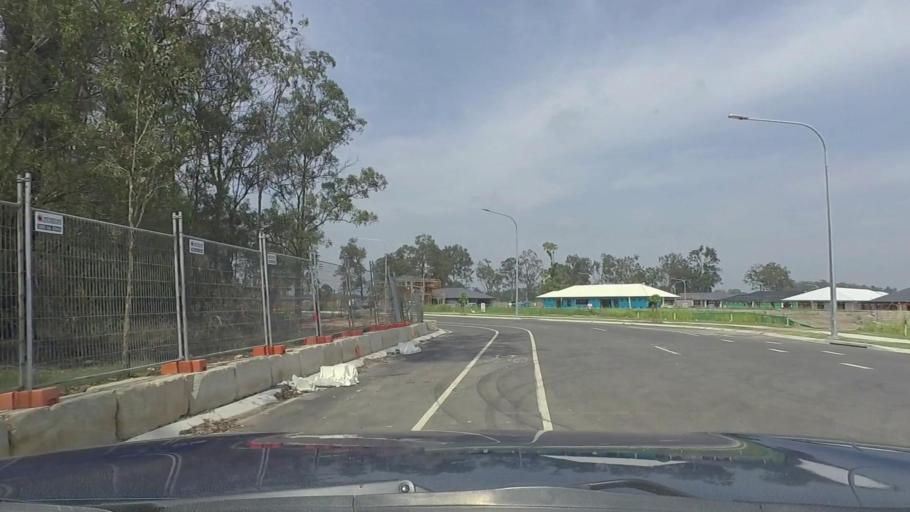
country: AU
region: Queensland
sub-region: Logan
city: Logan Reserve
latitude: -27.7041
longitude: 153.1071
